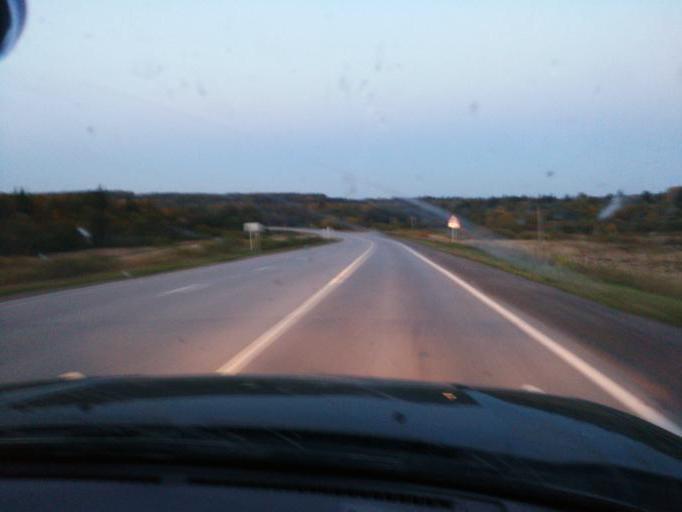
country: RU
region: Perm
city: Verkhnechusovskiye Gorodki
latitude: 58.2647
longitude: 57.3328
